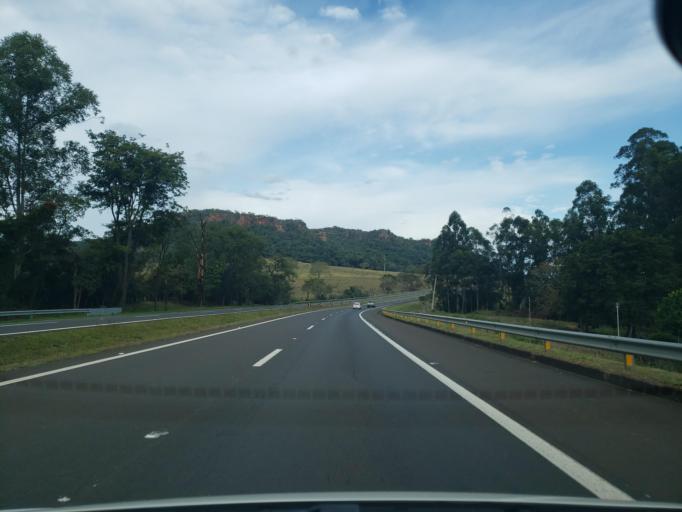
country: BR
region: Sao Paulo
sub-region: Itirapina
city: Itirapina
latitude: -22.2731
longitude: -47.9438
